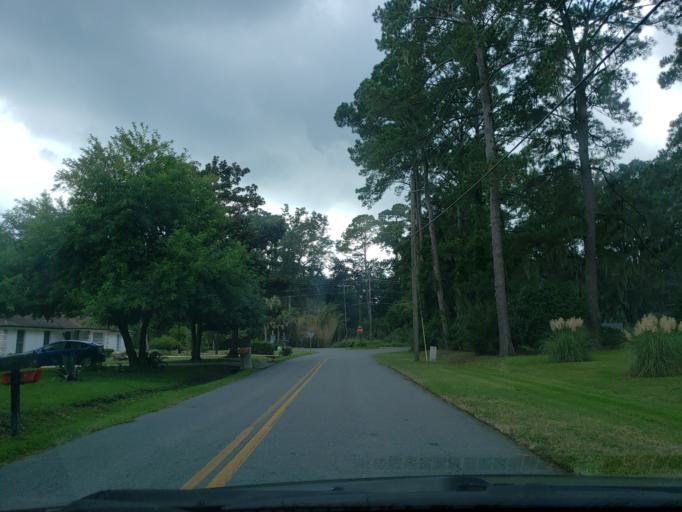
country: US
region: Georgia
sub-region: Chatham County
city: Montgomery
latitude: 31.9315
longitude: -81.0927
